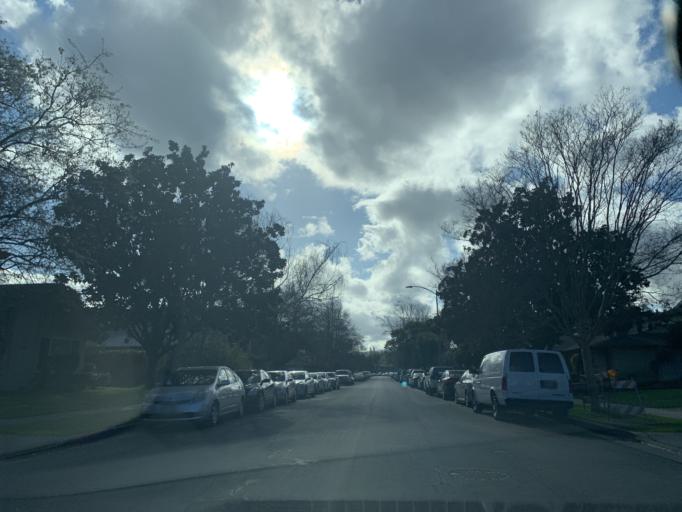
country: US
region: California
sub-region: Santa Clara County
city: Buena Vista
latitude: 37.3032
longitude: -121.9241
